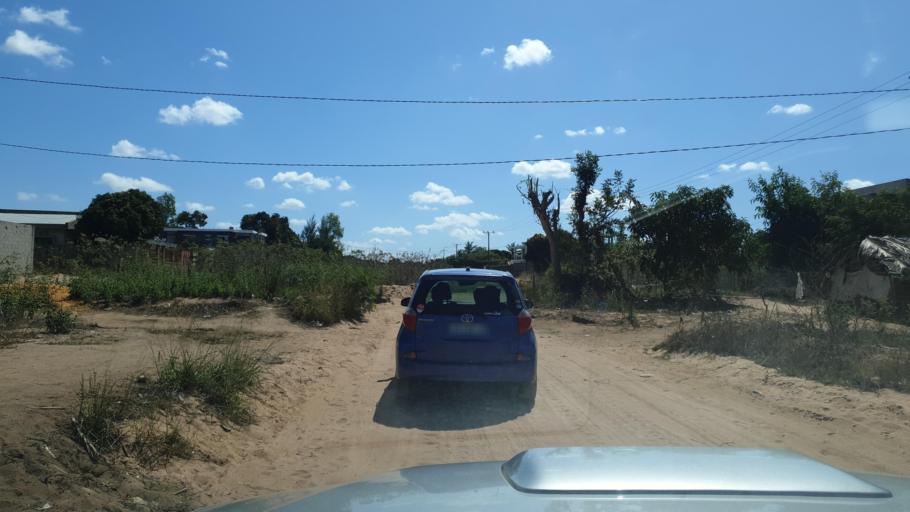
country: MZ
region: Nampula
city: Nampula
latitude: -15.1065
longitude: 39.2061
